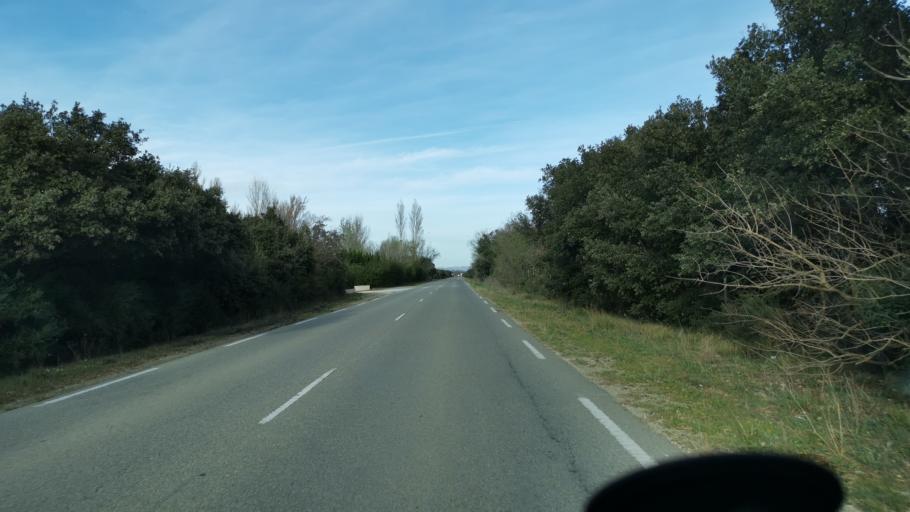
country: FR
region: Provence-Alpes-Cote d'Azur
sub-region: Departement des Bouches-du-Rhone
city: Saint-Martin-de-Crau
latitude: 43.5786
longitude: 4.7558
